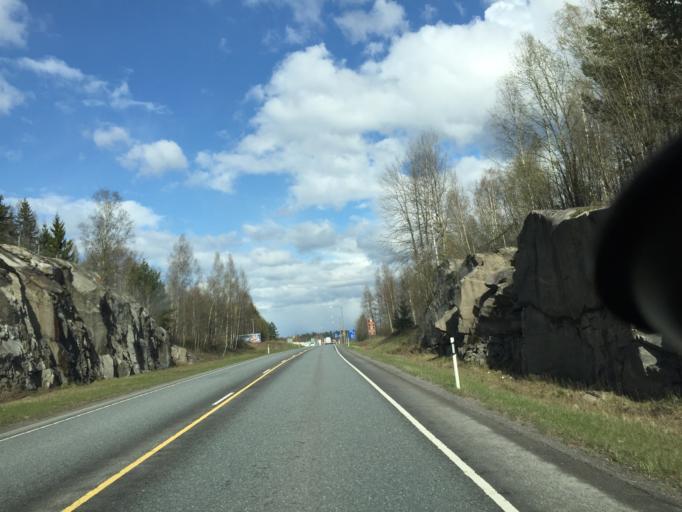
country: FI
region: Uusimaa
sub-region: Raaseporin
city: Karis
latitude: 60.0499
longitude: 23.6406
